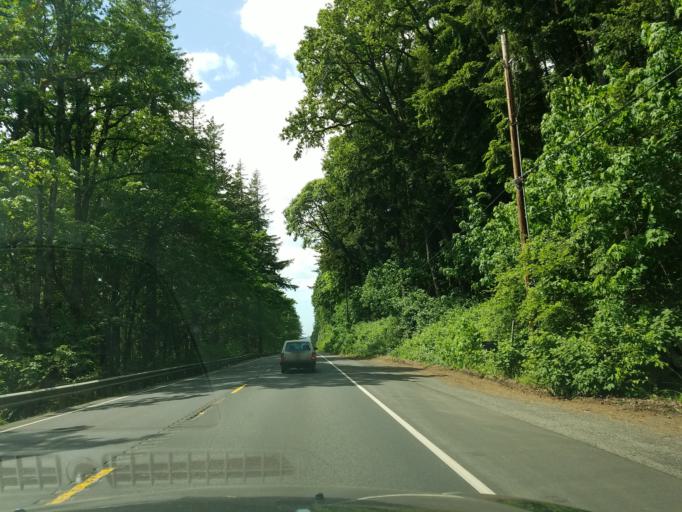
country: US
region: Washington
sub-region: Clark County
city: Washougal
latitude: 45.5668
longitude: -122.2843
